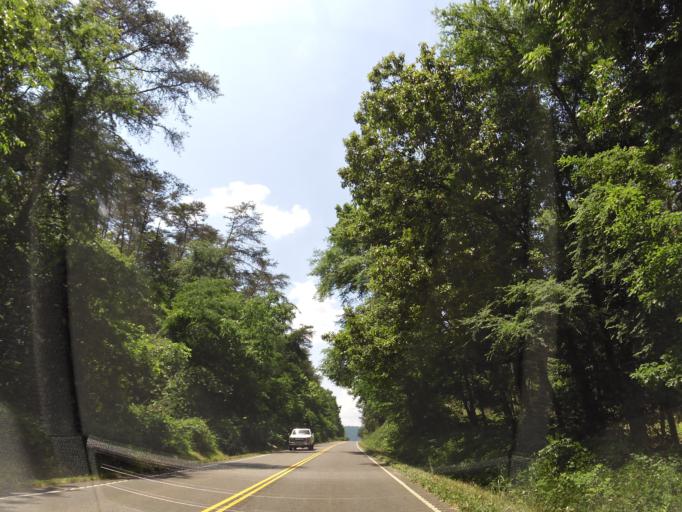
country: US
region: Tennessee
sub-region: Rhea County
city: Spring City
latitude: 35.6482
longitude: -84.8640
